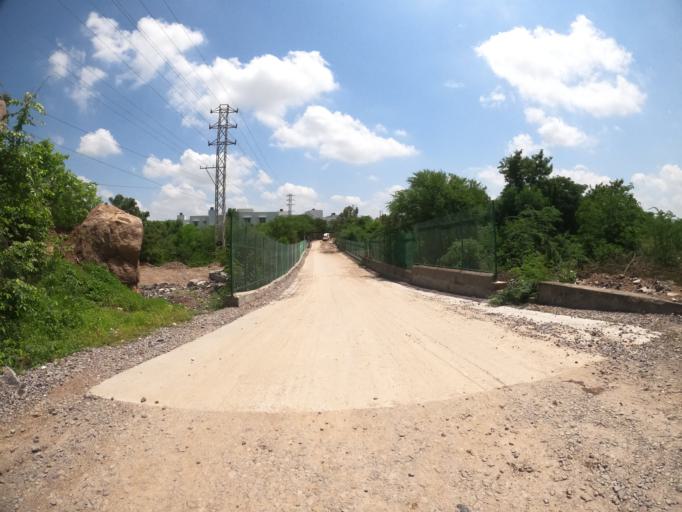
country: IN
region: Telangana
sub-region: Medak
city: Serilingampalle
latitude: 17.3785
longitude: 78.3225
